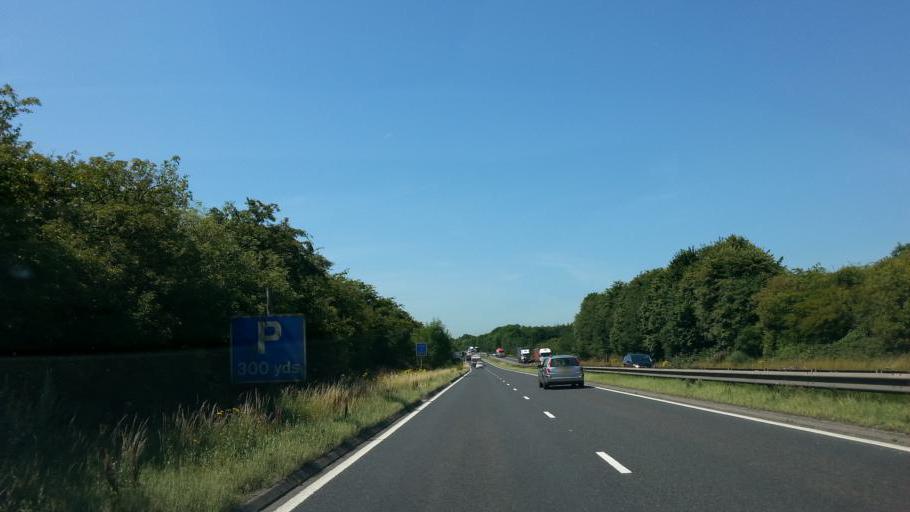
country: GB
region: England
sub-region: Derbyshire
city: Blackwell
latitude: 53.0929
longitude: -1.3539
